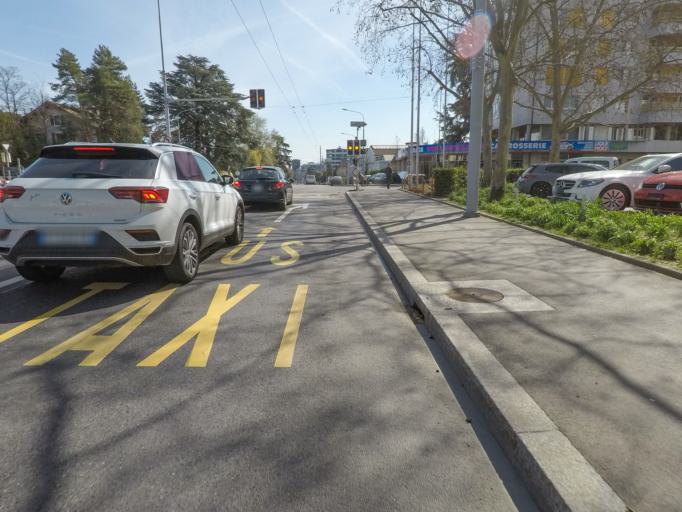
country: CH
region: Geneva
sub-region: Geneva
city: Les Avanchets
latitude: 46.2110
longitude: 6.1140
